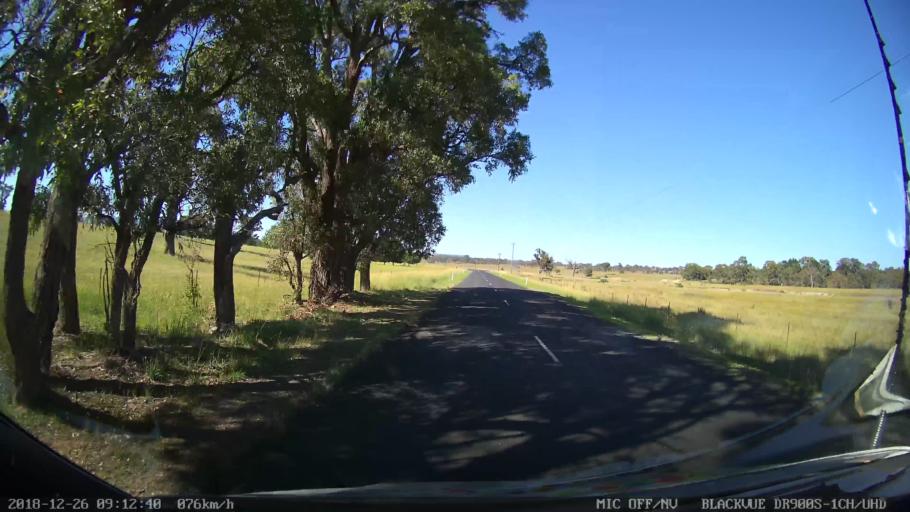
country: AU
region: New South Wales
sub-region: Mid-Western Regional
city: Kandos
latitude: -32.7600
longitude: 149.9806
